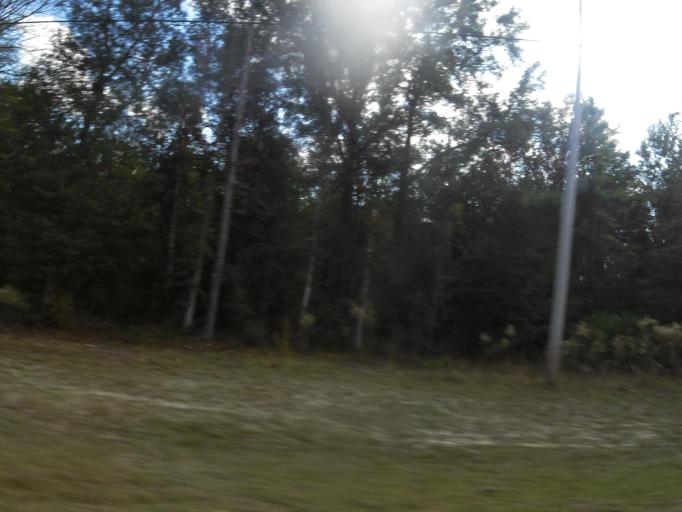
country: US
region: Florida
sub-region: Clay County
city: Middleburg
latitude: 30.1589
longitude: -81.9684
